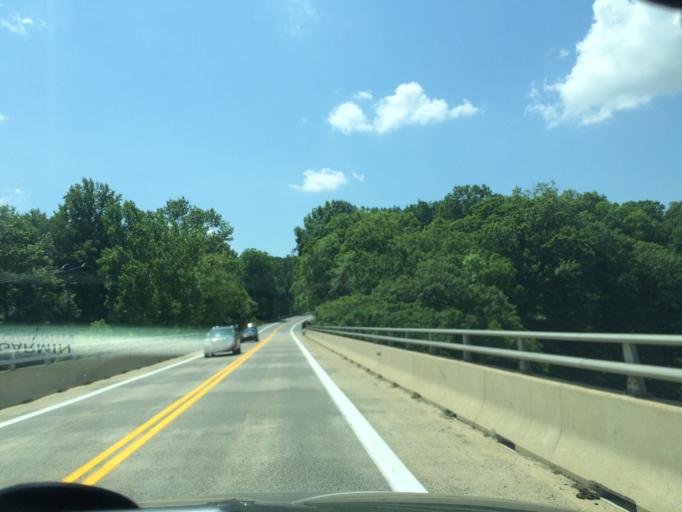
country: US
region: Maryland
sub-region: Carroll County
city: Eldersburg
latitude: 39.4362
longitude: -76.9369
